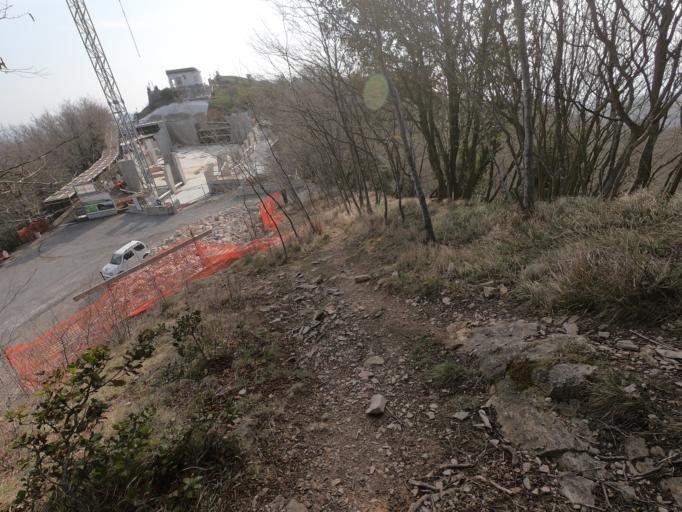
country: IT
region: Liguria
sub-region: Provincia di Savona
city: Balestrino
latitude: 44.1112
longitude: 8.1618
